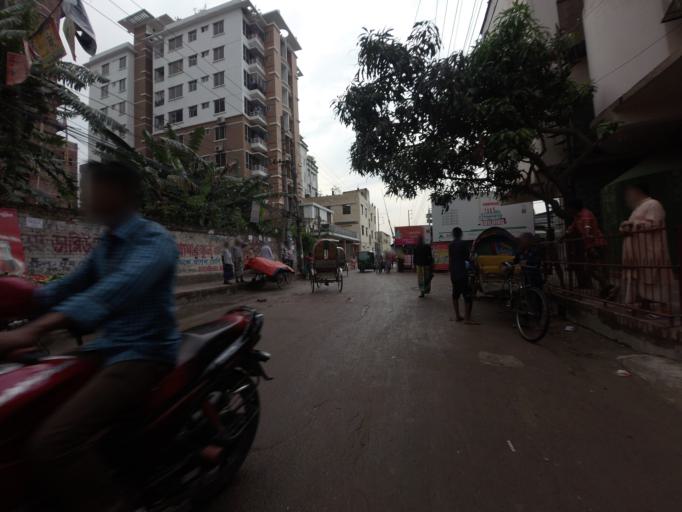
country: BD
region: Dhaka
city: Azimpur
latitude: 23.7755
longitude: 90.3527
